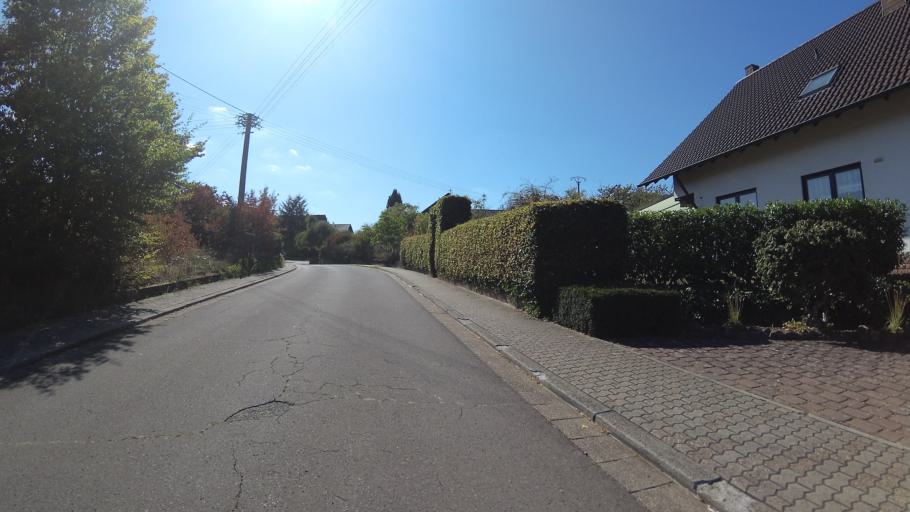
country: DE
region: Saarland
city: Lebach
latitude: 49.3881
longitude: 6.9207
